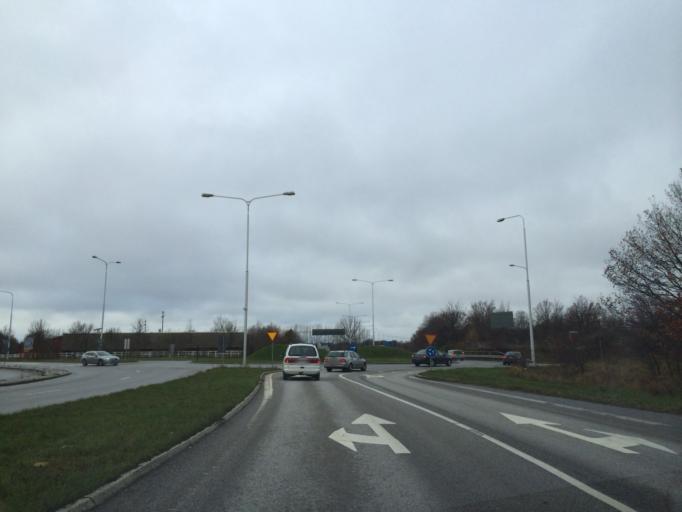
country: SE
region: Skane
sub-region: Lunds Kommun
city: Lund
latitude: 55.7194
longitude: 13.2144
